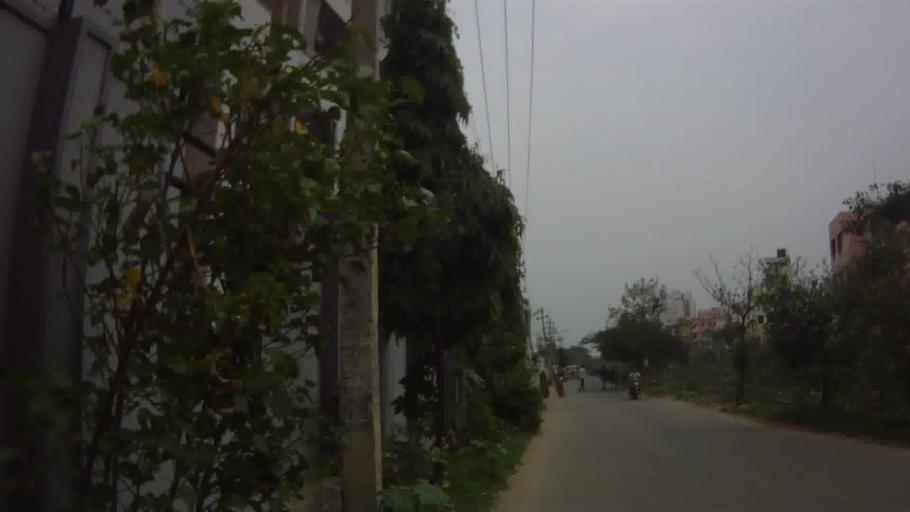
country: IN
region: Karnataka
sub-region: Bangalore Urban
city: Bangalore
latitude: 12.9617
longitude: 77.7040
